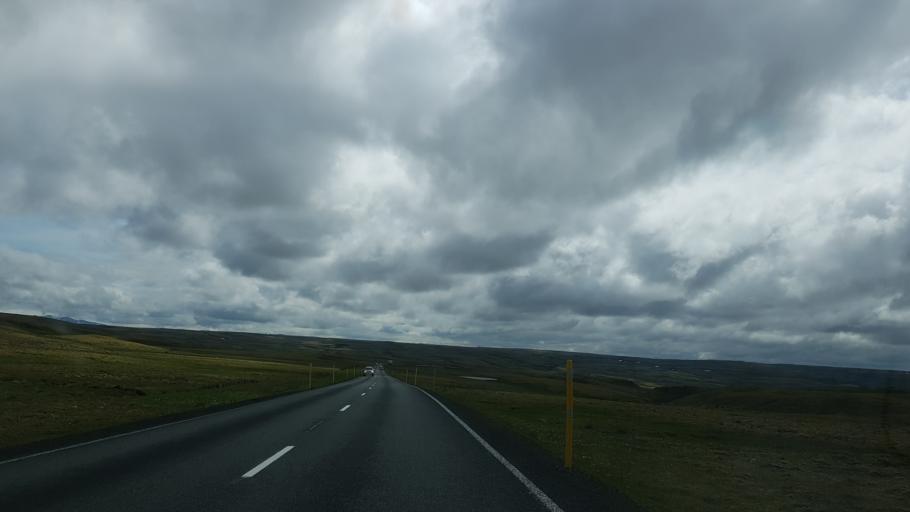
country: IS
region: West
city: Borgarnes
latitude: 64.9575
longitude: -21.0601
